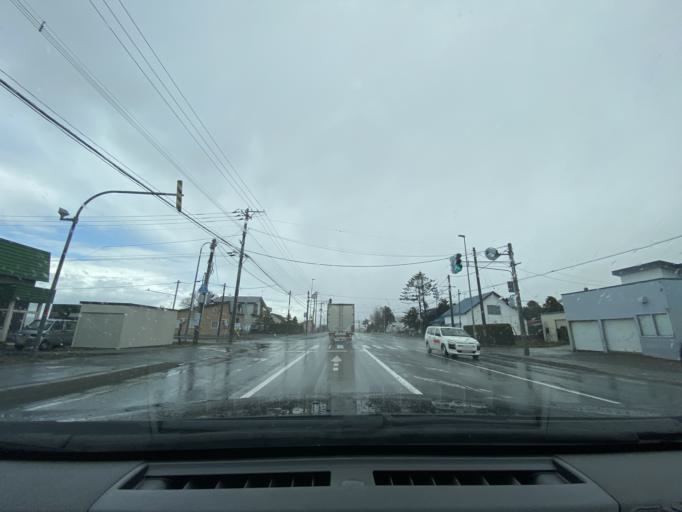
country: JP
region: Hokkaido
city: Fukagawa
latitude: 43.6615
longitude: 141.9937
